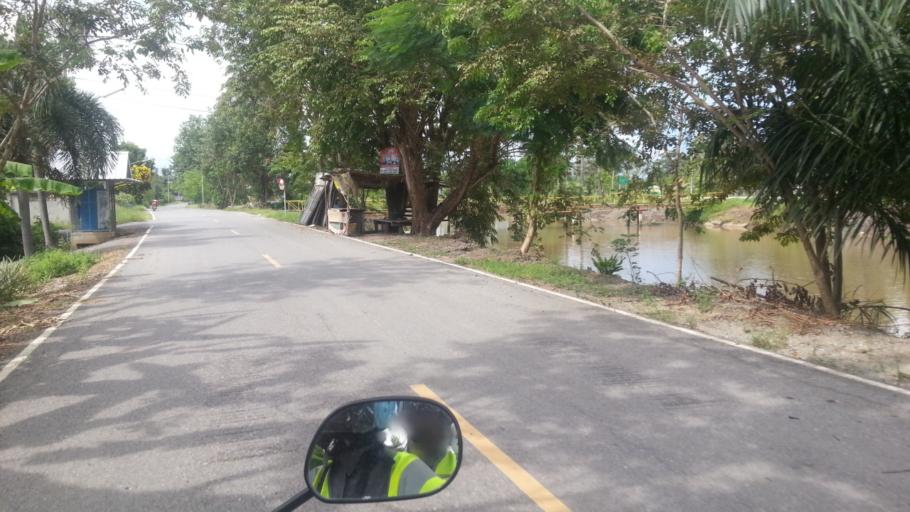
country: TH
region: Pathum Thani
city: Nong Suea
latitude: 14.0922
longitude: 100.8237
